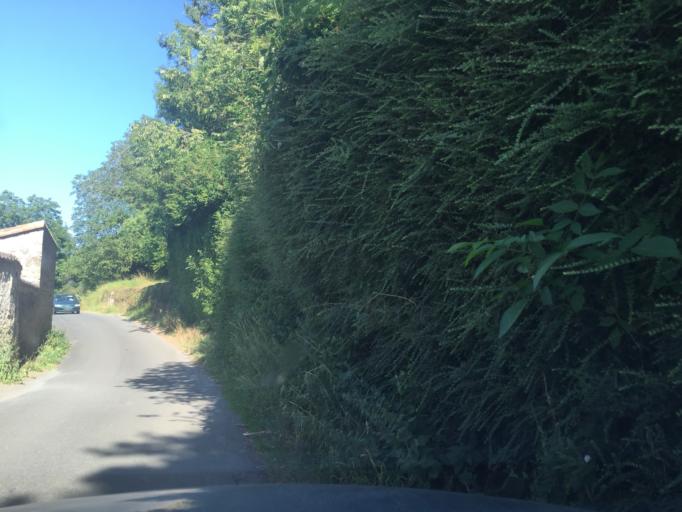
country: FR
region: Poitou-Charentes
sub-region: Departement de la Vienne
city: Lusignan
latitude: 46.4379
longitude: 0.1274
